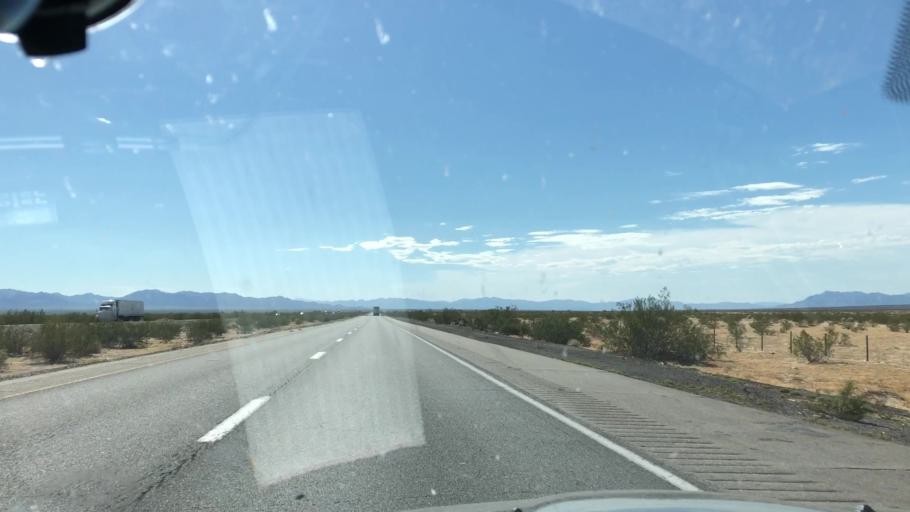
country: US
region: California
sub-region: Riverside County
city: Mesa Verde
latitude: 33.6259
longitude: -115.0546
